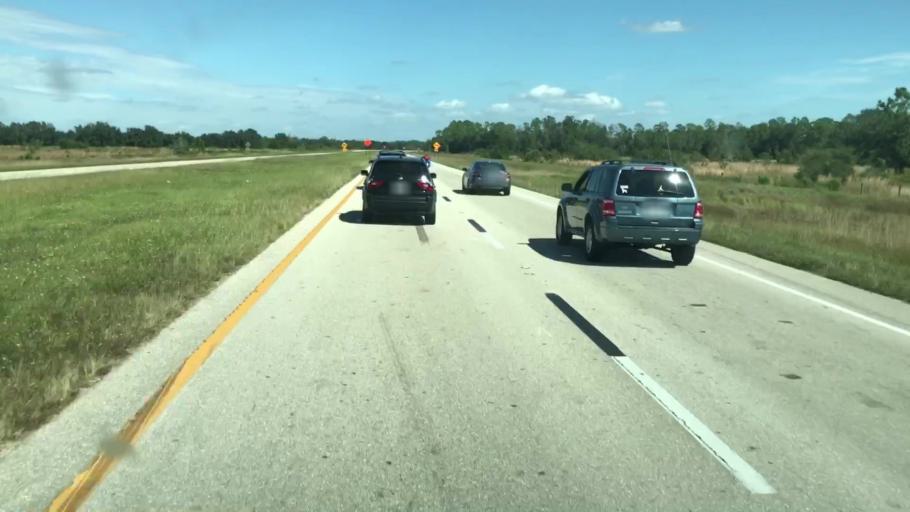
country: US
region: Florida
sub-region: Lee County
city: Gateway
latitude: 26.5707
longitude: -81.7266
